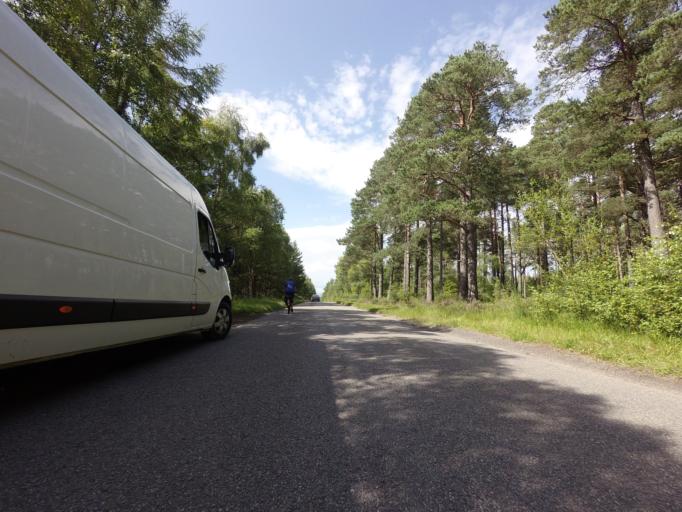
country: GB
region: Scotland
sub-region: Highland
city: Fortrose
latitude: 57.4806
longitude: -4.0886
